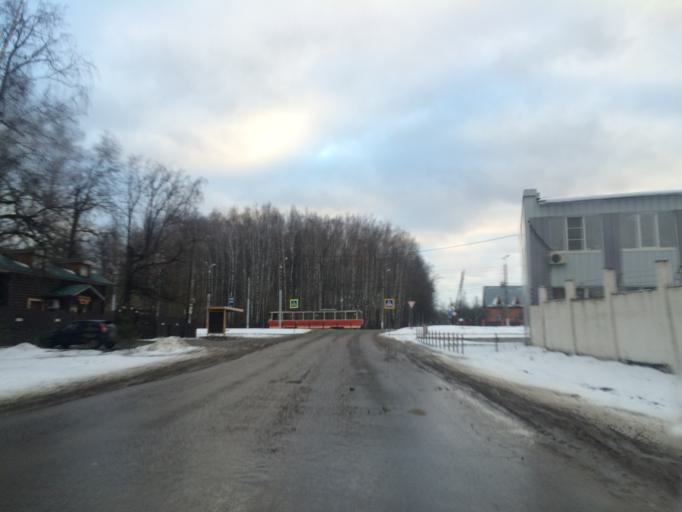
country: RU
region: Tula
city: Tula
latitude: 54.2200
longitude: 37.7040
